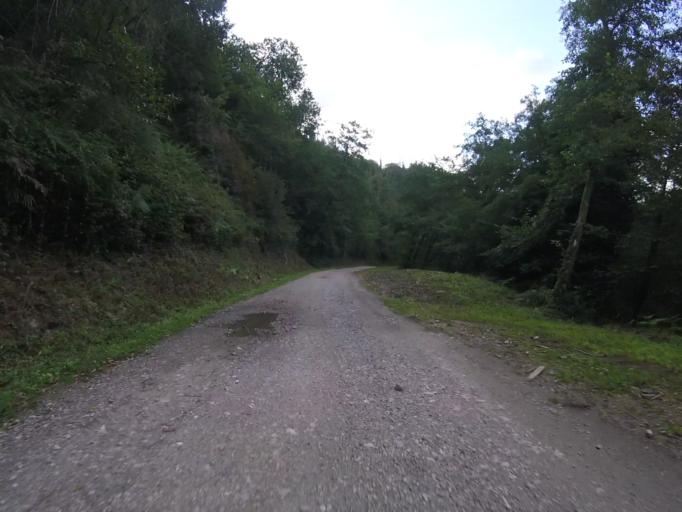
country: ES
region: Basque Country
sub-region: Provincia de Guipuzcoa
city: Elduayen
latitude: 43.1714
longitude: -1.9607
